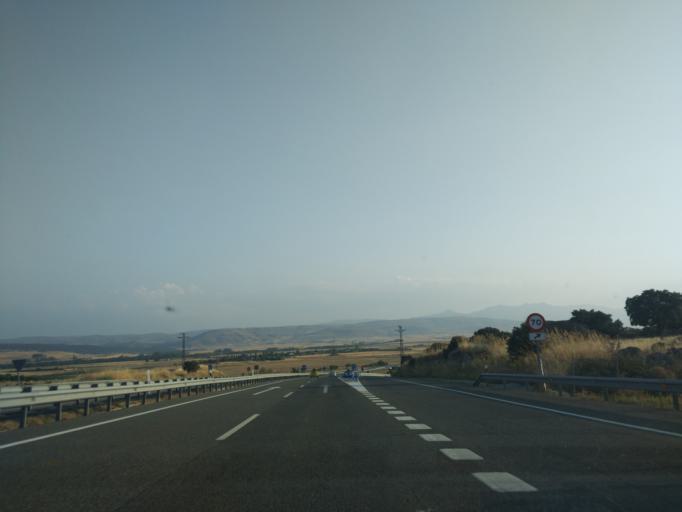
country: ES
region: Castille and Leon
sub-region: Provincia de Avila
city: Avila
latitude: 40.6528
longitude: -4.7246
